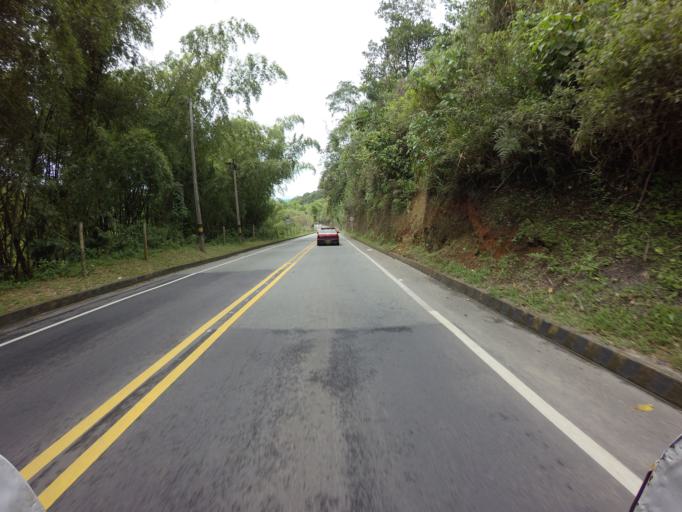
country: CO
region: Quindio
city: Quimbaya
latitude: 4.6138
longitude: -75.7725
